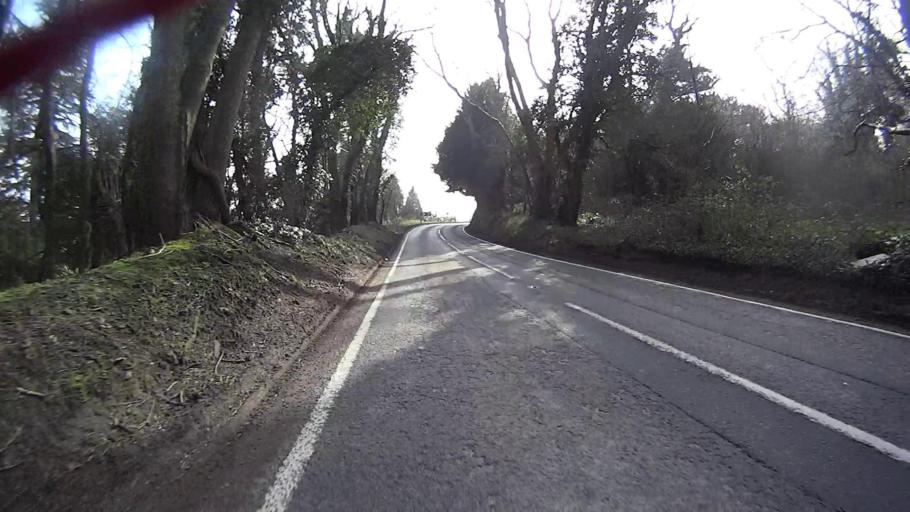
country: GB
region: England
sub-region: Surrey
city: Headley
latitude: 51.2555
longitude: -0.2618
